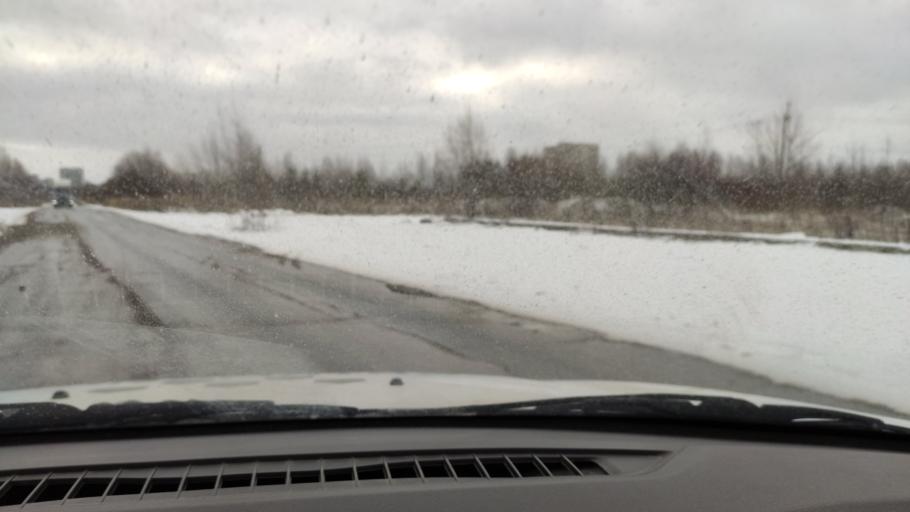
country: RU
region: Perm
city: Perm
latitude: 58.0364
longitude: 56.1908
